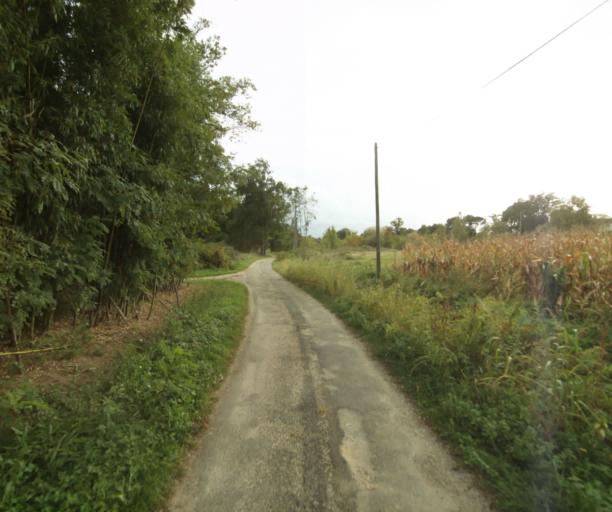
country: FR
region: Aquitaine
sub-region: Departement des Landes
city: Gabarret
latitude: 43.9562
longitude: 0.0985
